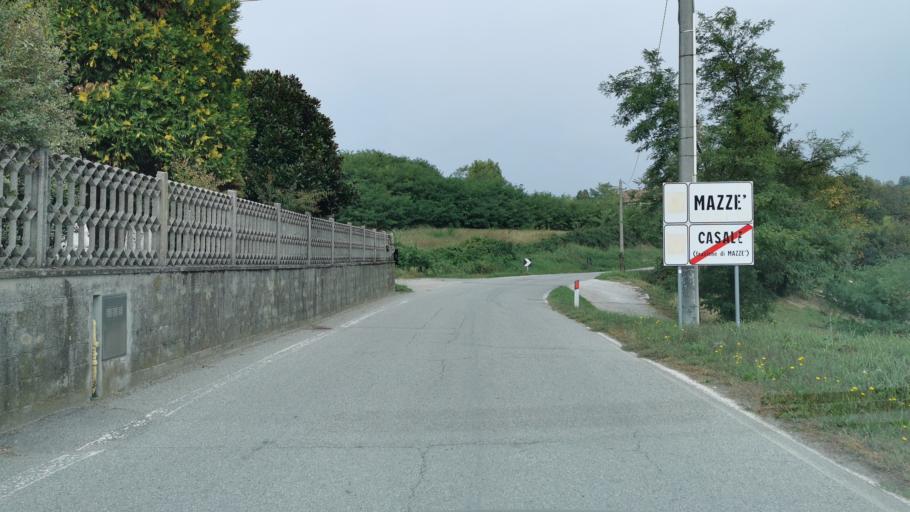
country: IT
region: Piedmont
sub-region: Provincia di Torino
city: Tonengo-Casale
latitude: 45.2946
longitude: 7.9419
